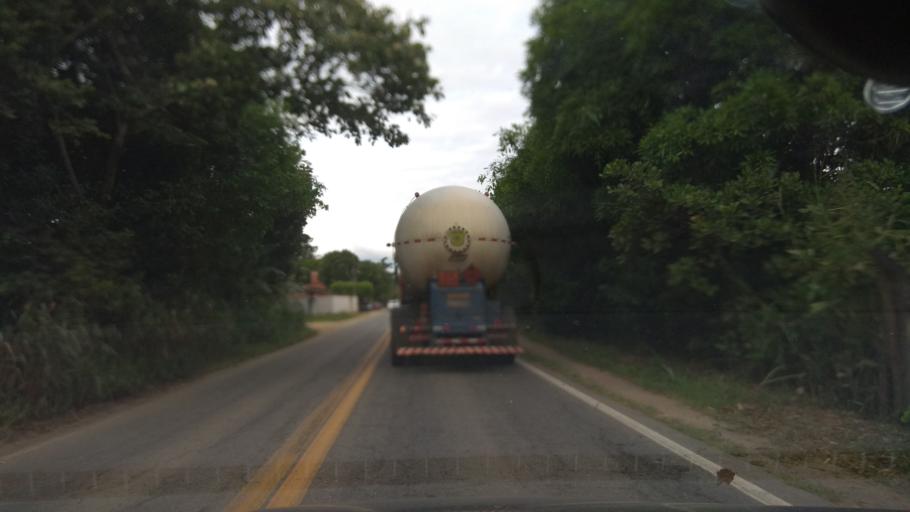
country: BR
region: Bahia
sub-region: Ipiau
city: Ipiau
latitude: -14.1646
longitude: -39.6888
